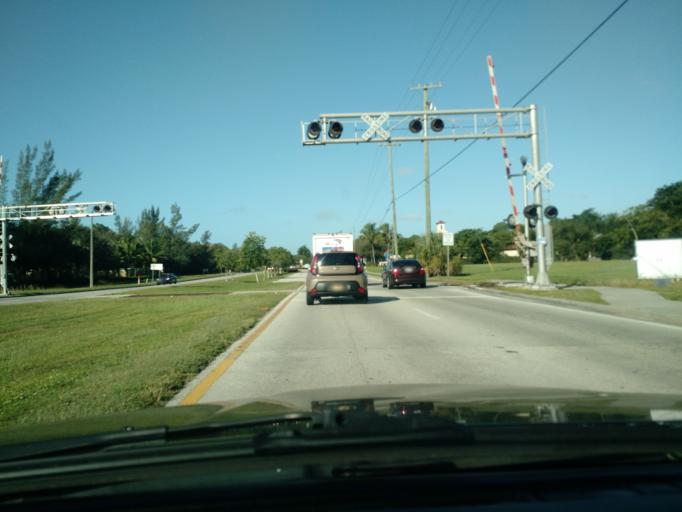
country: US
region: Florida
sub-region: Lee County
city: Bonita Springs
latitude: 26.3311
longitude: -81.7821
